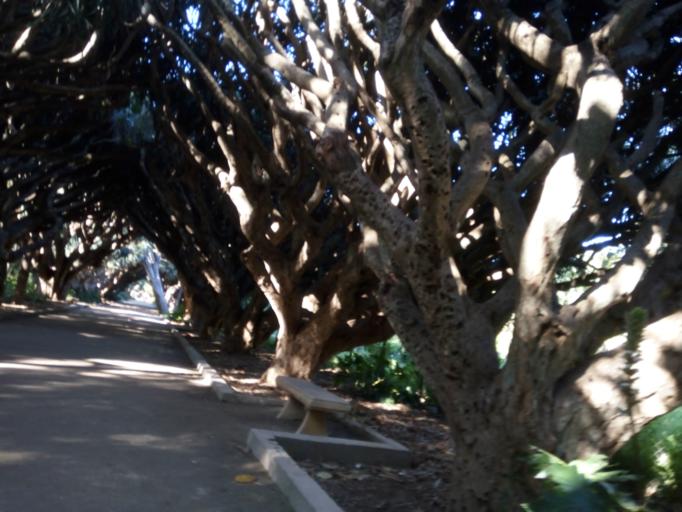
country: DZ
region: Alger
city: Algiers
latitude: 36.7473
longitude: 3.0752
